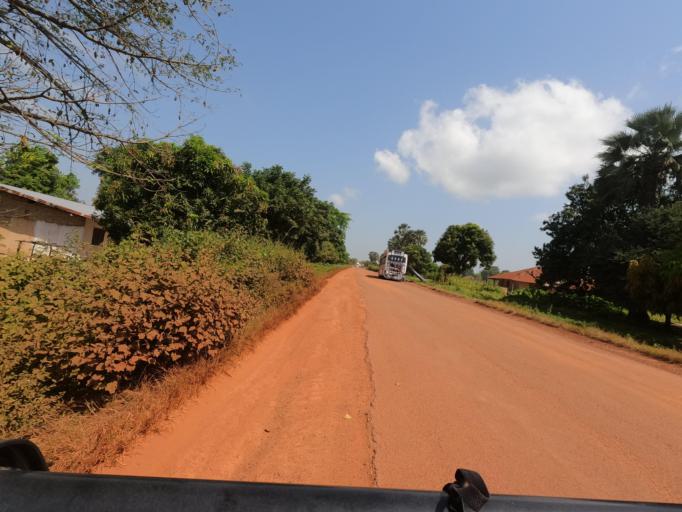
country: GW
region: Cacheu
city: Canchungo
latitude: 12.2796
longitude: -15.7856
